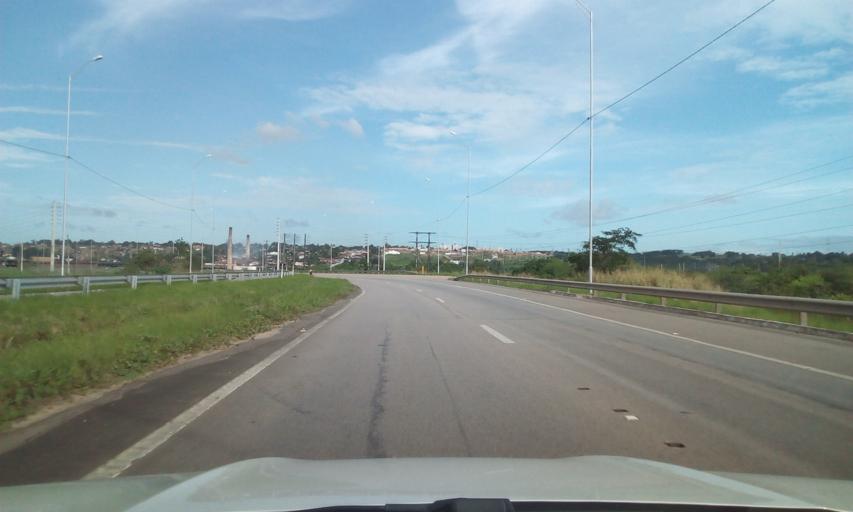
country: BR
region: Paraiba
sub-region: Santa Rita
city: Santa Rita
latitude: -7.1121
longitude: -34.9618
